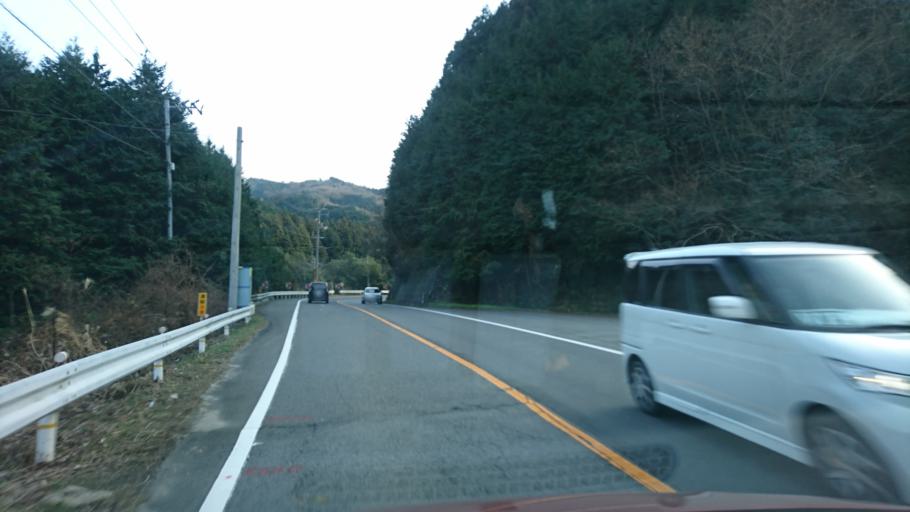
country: JP
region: Ehime
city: Hojo
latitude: 33.9849
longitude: 132.9084
